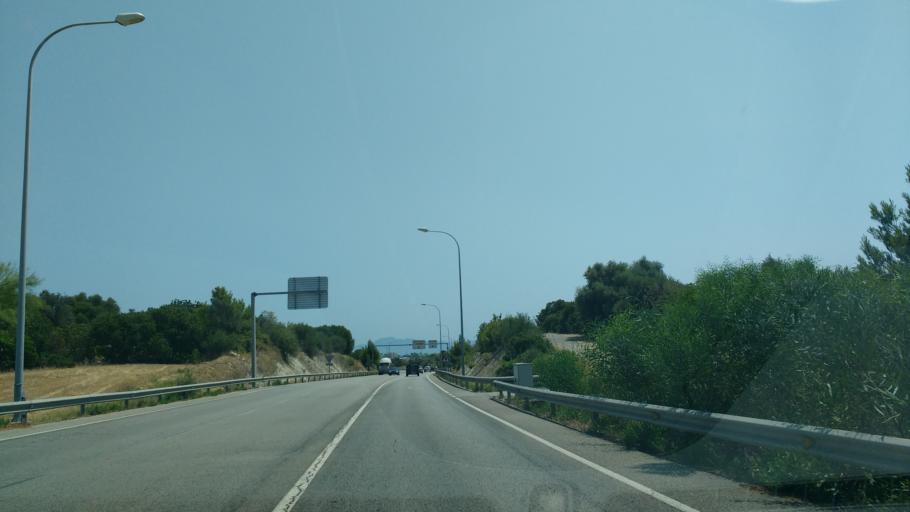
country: ES
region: Balearic Islands
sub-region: Illes Balears
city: Alcudia
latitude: 39.8441
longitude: 3.0947
